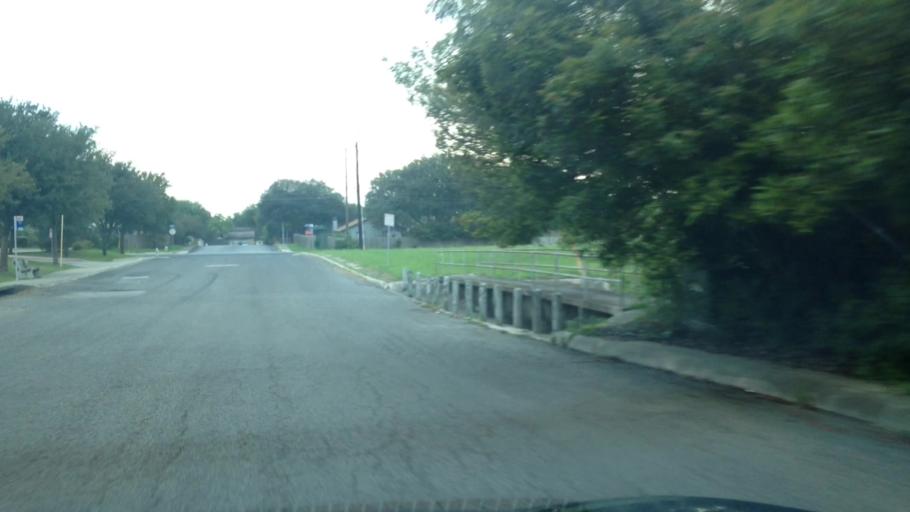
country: US
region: Texas
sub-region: Bexar County
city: Live Oak
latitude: 29.5902
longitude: -98.3781
